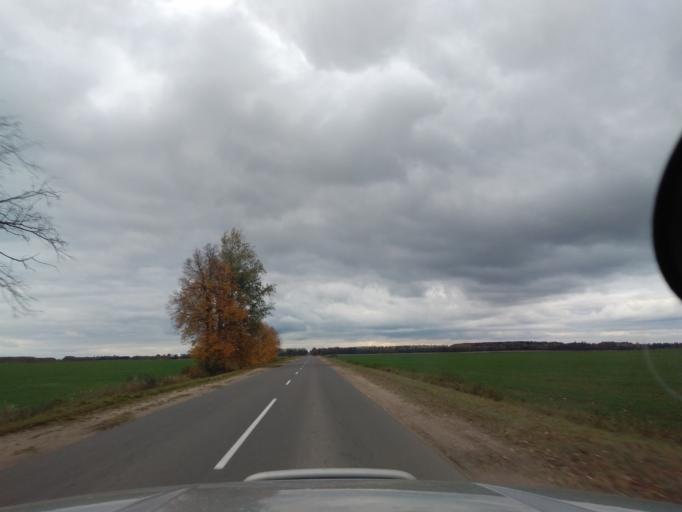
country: BY
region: Minsk
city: Slutsk
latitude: 53.2076
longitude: 27.3669
